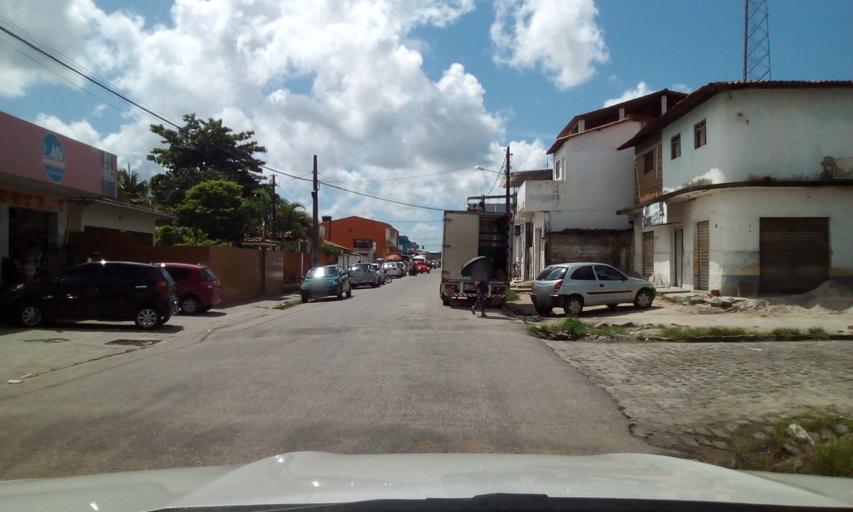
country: BR
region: Paraiba
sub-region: Bayeux
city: Bayeux
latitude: -7.1330
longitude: -34.9277
